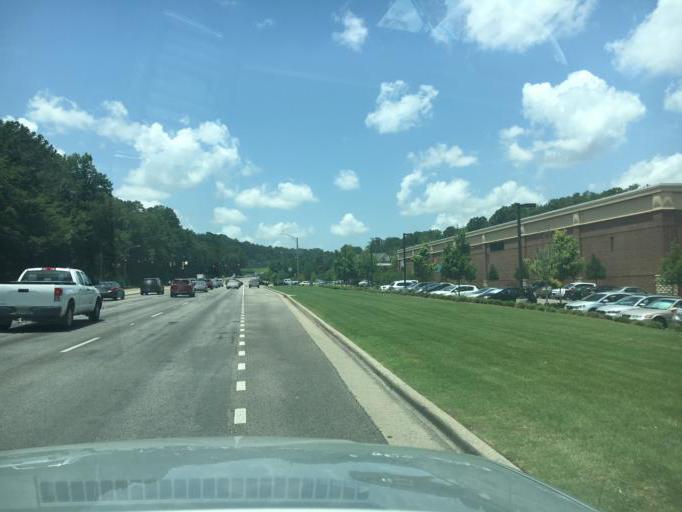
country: US
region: Alabama
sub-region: Jefferson County
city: Cahaba Heights
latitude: 33.4590
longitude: -86.7522
